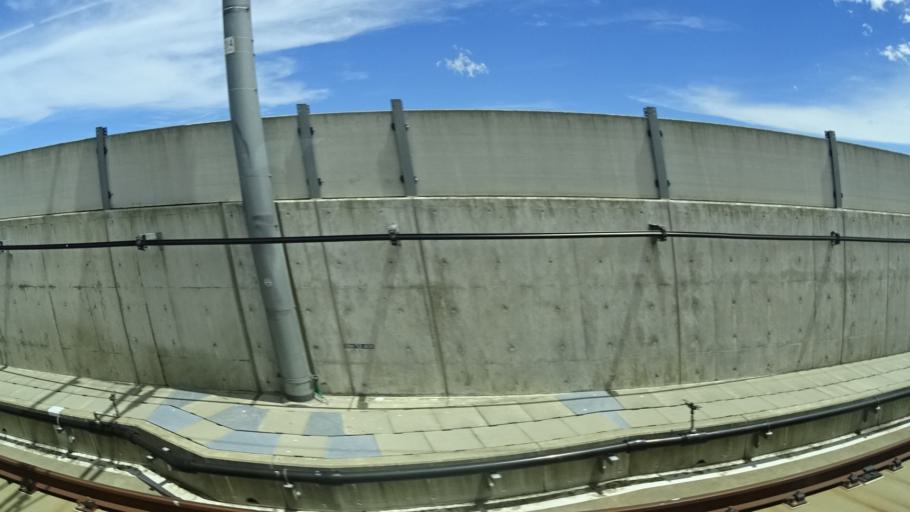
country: JP
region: Niigata
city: Joetsu
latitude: 37.0767
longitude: 138.2534
